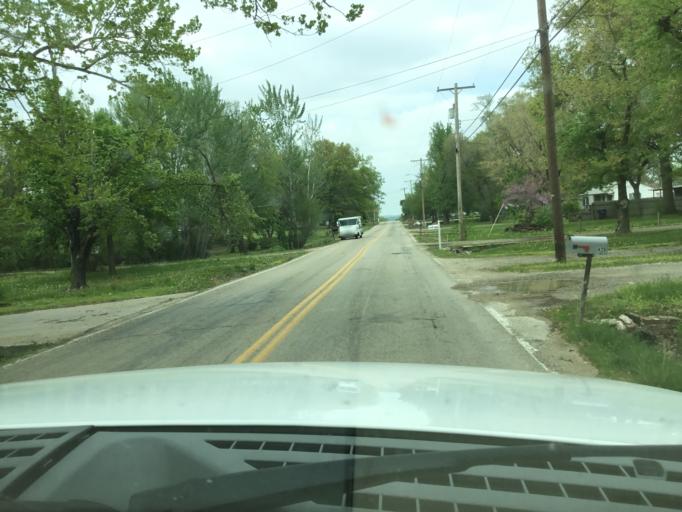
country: US
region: Kansas
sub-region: Shawnee County
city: Topeka
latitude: 39.0466
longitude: -95.6227
